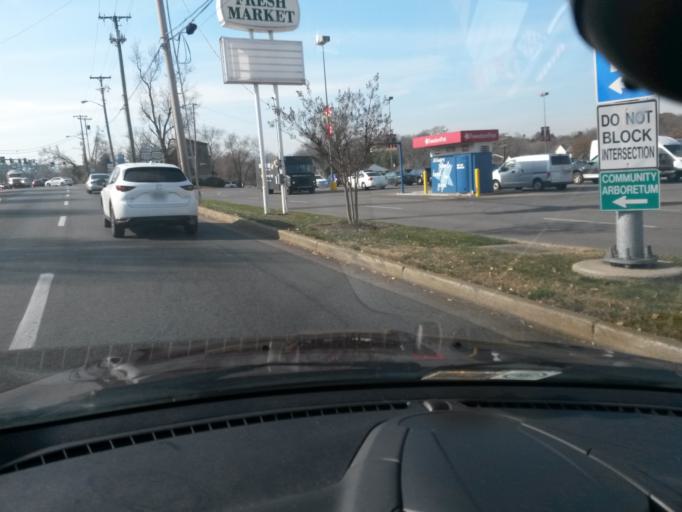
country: US
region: Virginia
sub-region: City of Roanoke
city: Roanoke
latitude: 37.2542
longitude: -79.9570
